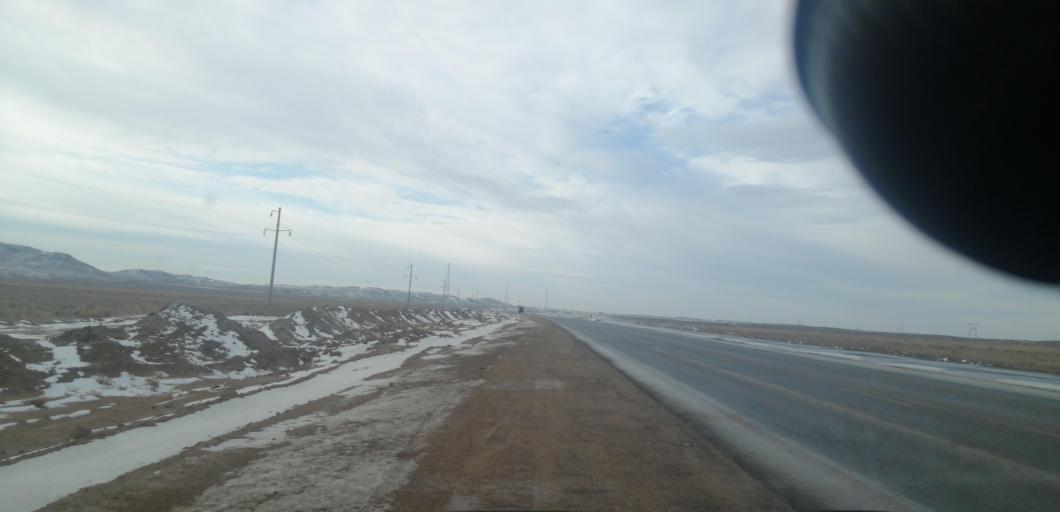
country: KZ
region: Qaraghandy
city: Balqash
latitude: 46.6498
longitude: 74.3898
